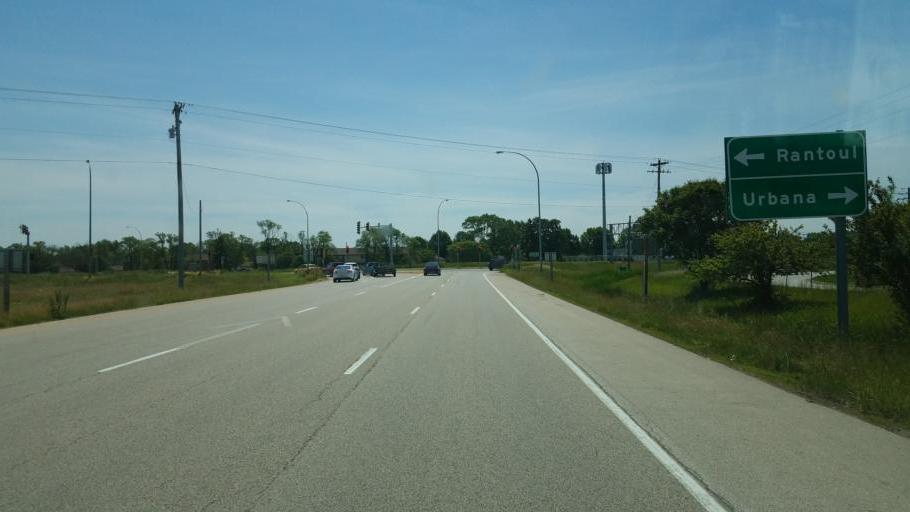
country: US
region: Illinois
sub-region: Champaign County
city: Urbana
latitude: 40.1331
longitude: -88.1974
